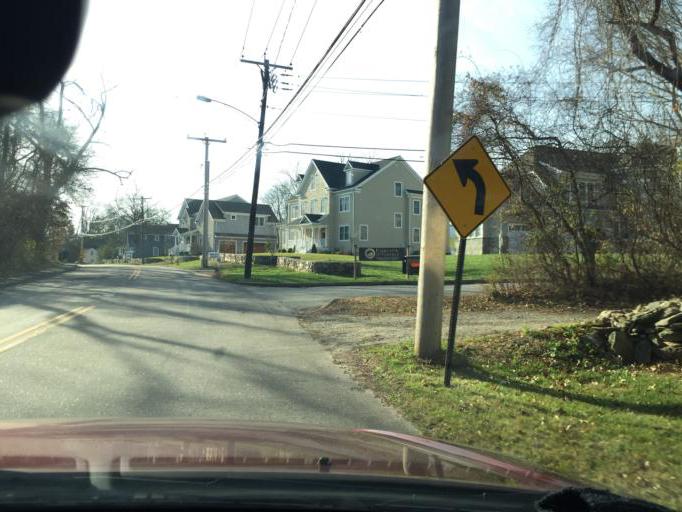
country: US
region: Connecticut
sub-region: Fairfield County
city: Southport
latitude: 41.1445
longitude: -73.2864
